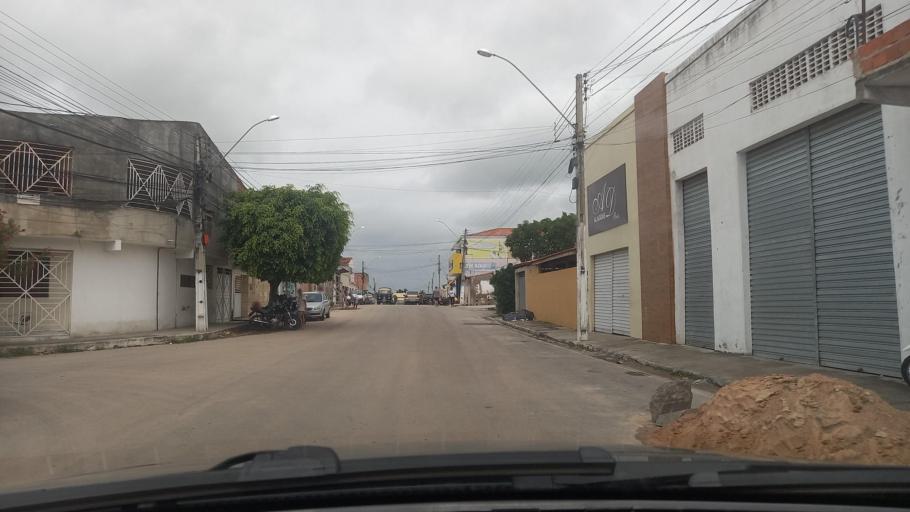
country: BR
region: Alagoas
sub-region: Delmiro Gouveia
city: Delmiro Gouveia
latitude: -9.3879
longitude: -37.9989
